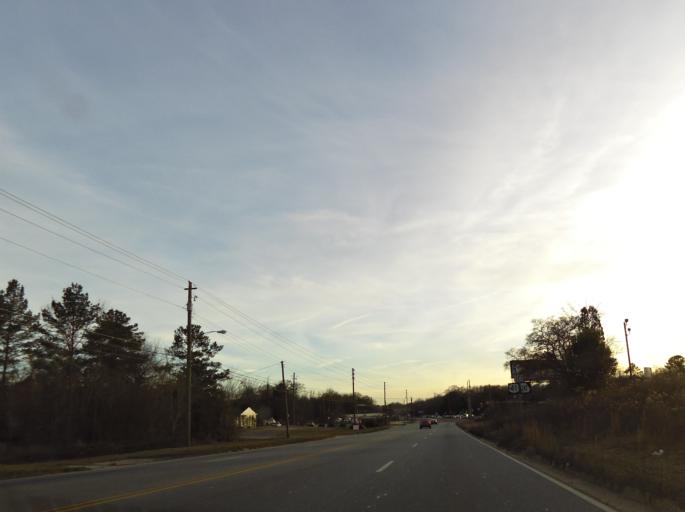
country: US
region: Georgia
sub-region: Bibb County
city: Macon
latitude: 32.7741
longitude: -83.6582
